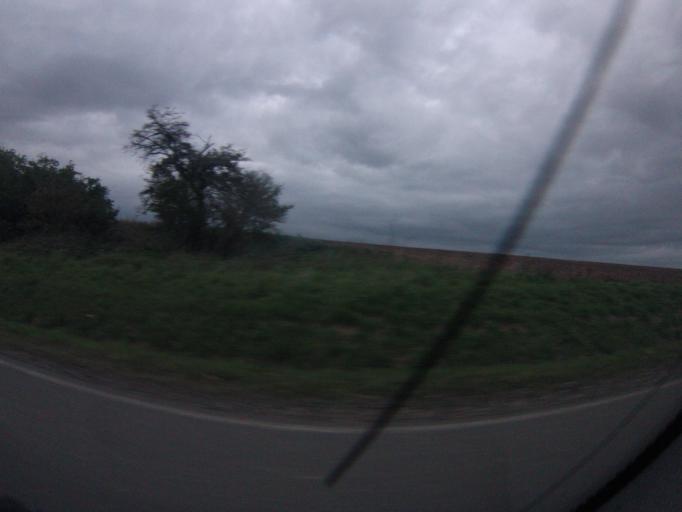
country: DE
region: Thuringia
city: Saara
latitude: 50.9179
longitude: 12.3961
